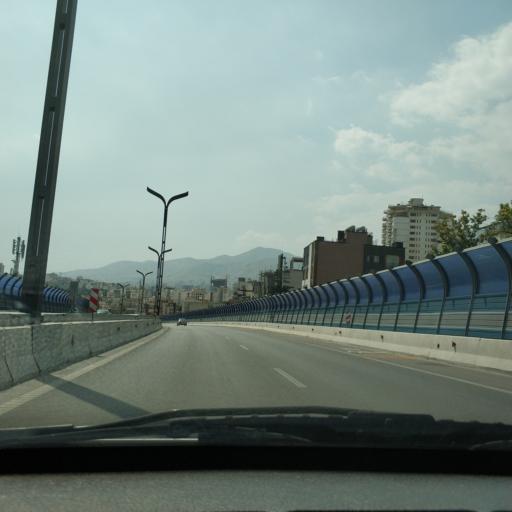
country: IR
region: Tehran
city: Tajrish
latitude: 35.7930
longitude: 51.4631
